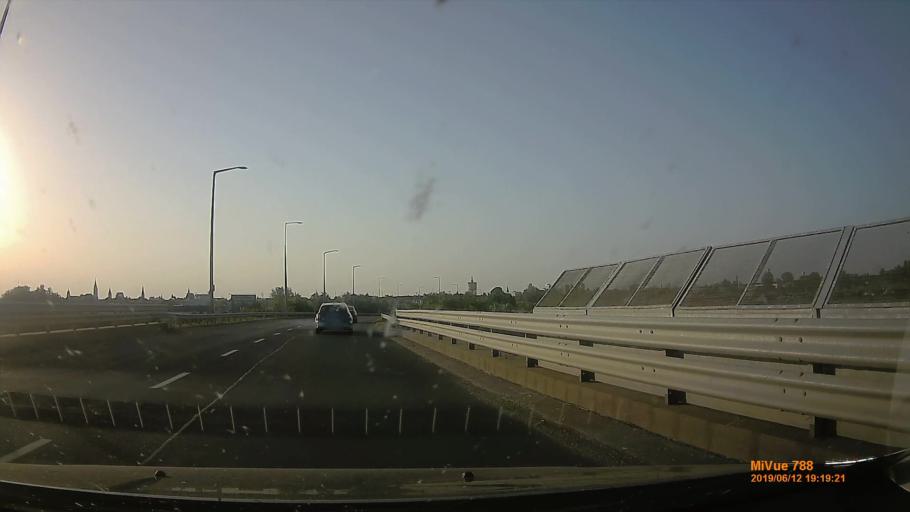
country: HU
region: Bacs-Kiskun
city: Kecskemet
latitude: 46.8981
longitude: 19.7040
